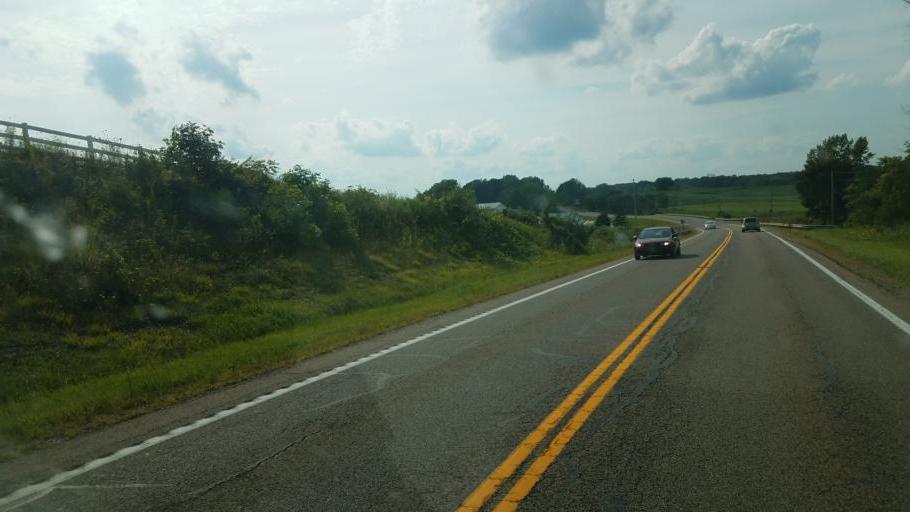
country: US
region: Ohio
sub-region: Morrow County
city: Mount Gilead
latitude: 40.5427
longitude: -82.7858
